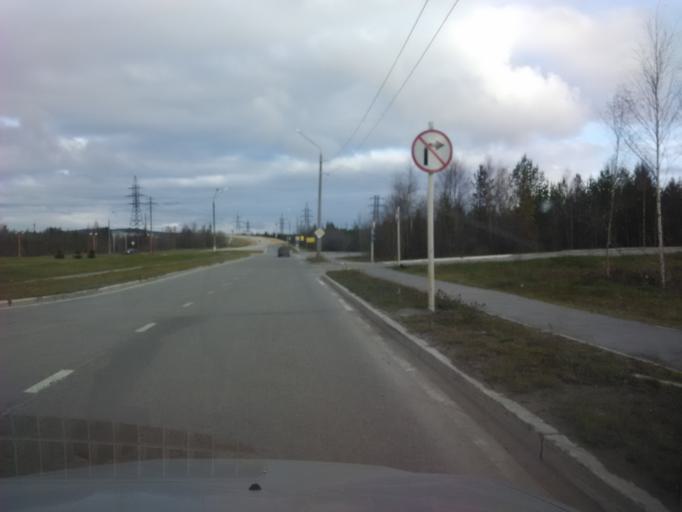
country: RU
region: Murmansk
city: Polyarnyye Zori
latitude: 67.3722
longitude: 32.5064
